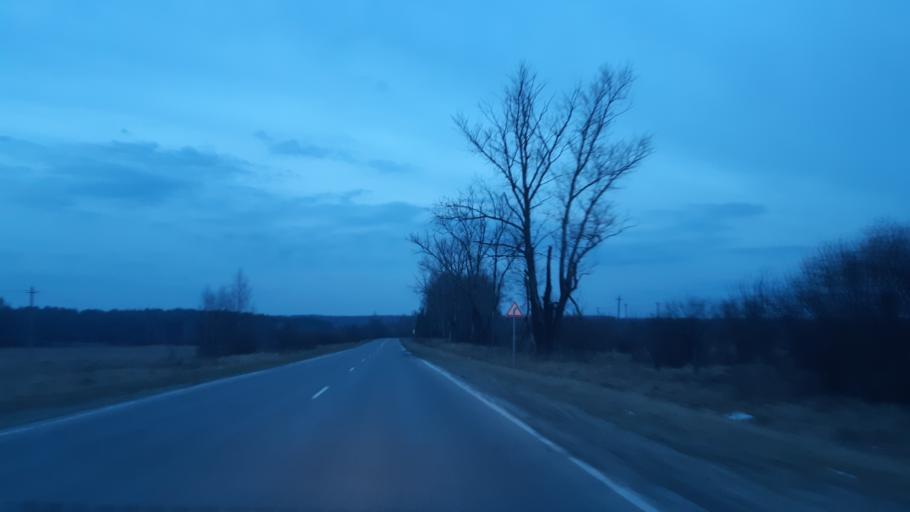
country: RU
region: Vladimir
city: Nikologory
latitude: 56.1708
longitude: 42.0006
